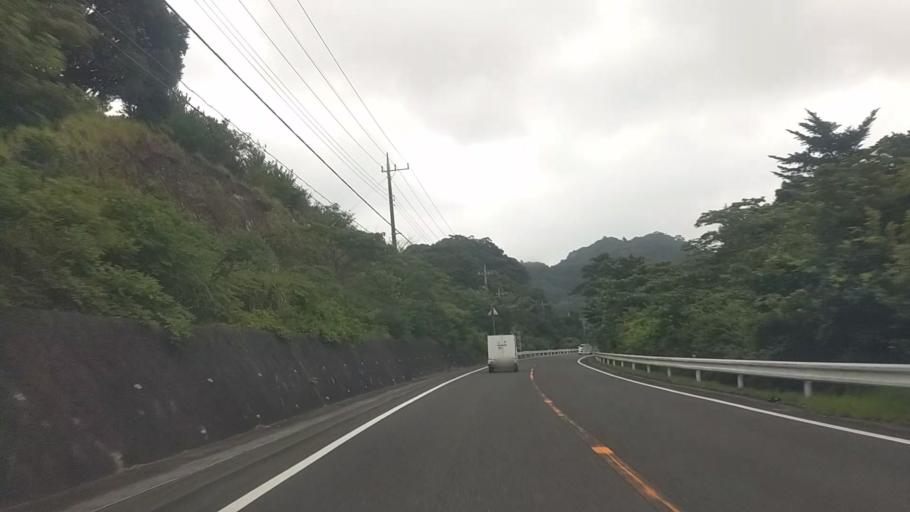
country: JP
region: Chiba
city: Kawaguchi
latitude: 35.1603
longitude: 140.0649
